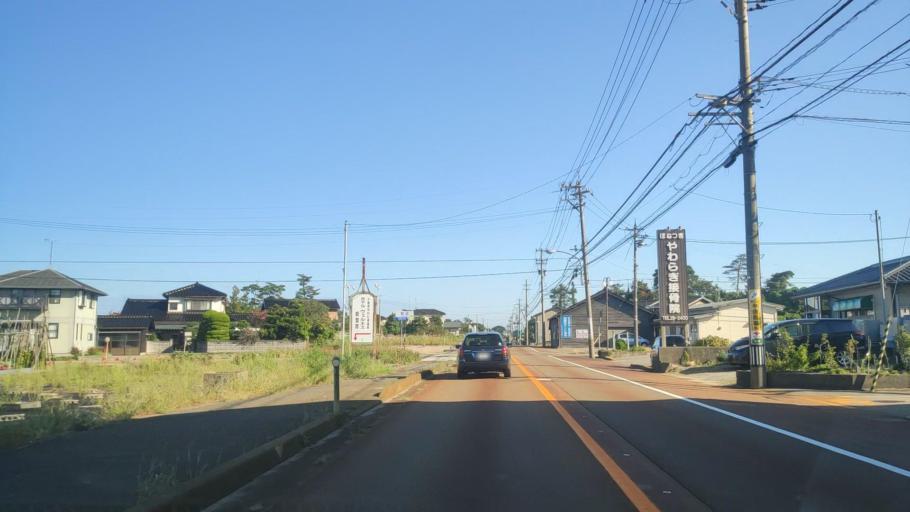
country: JP
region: Ishikawa
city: Hakui
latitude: 36.8532
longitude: 136.7693
